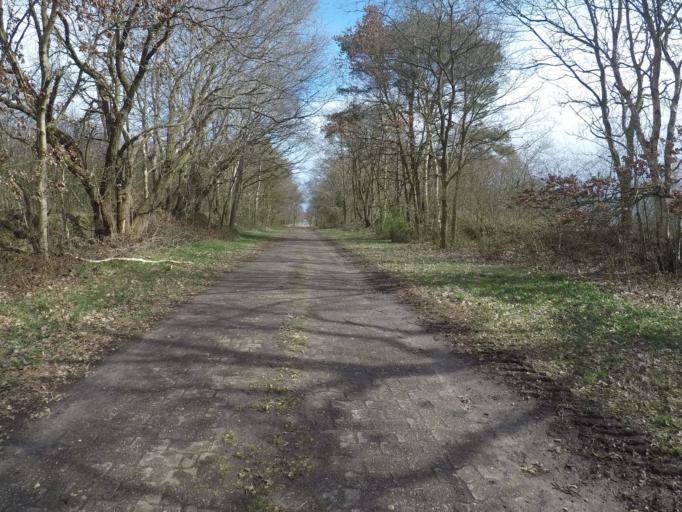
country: DE
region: Lower Saxony
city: Elmlohe
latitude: 53.6034
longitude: 8.6917
